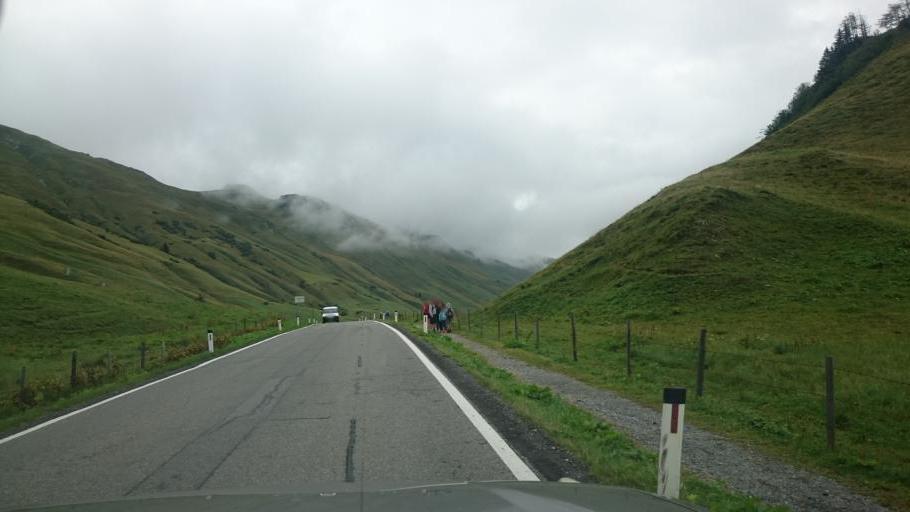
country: AT
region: Vorarlberg
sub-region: Politischer Bezirk Bregenz
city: Schroecken
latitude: 47.2694
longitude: 10.1301
